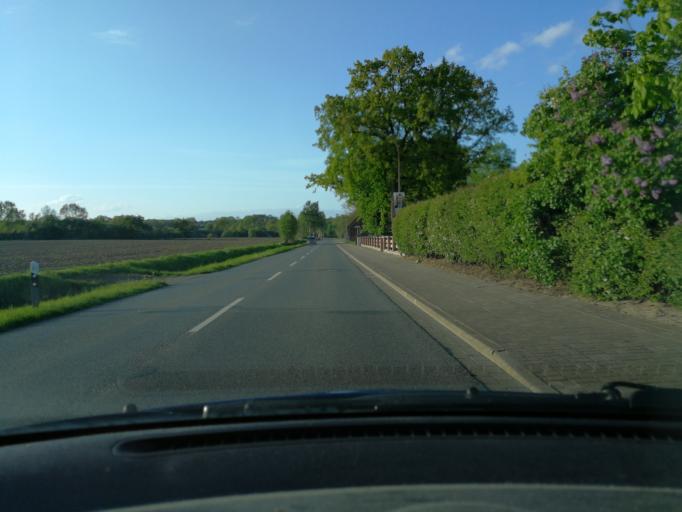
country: DE
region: Lower Saxony
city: Emmendorf
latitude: 53.0353
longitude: 10.5753
